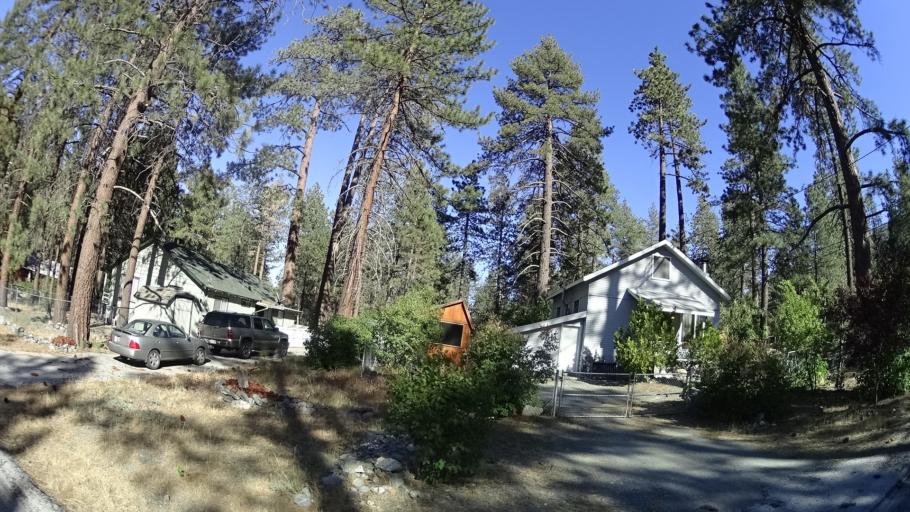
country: US
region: California
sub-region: San Bernardino County
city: Wrightwood
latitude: 34.3583
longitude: -117.6291
